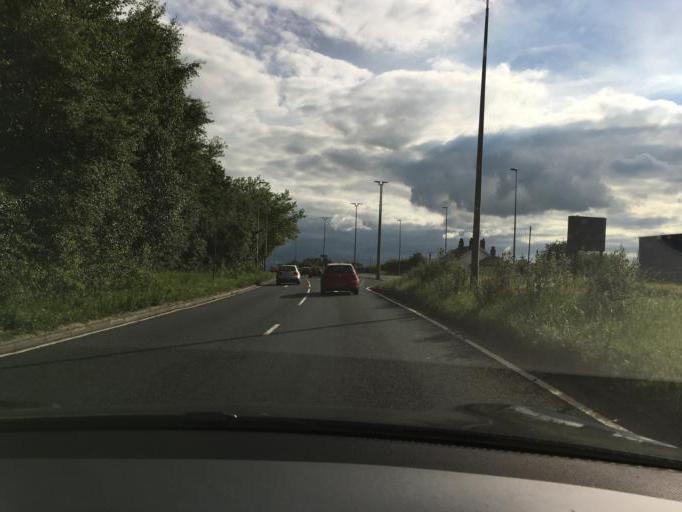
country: GB
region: England
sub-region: Trafford
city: Carrington
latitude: 53.4672
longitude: -2.3923
